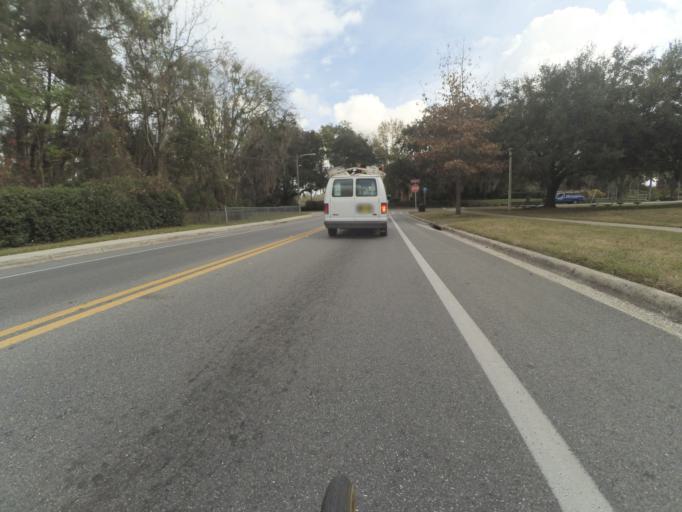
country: US
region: Florida
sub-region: Alachua County
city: Gainesville
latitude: 29.6422
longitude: -82.3647
